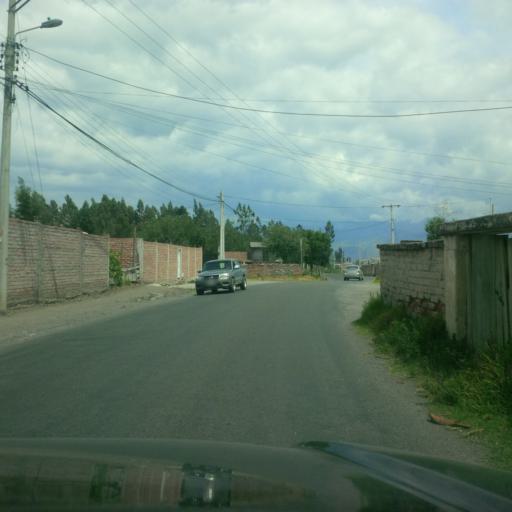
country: EC
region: Chimborazo
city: Riobamba
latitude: -1.6436
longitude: -78.6652
